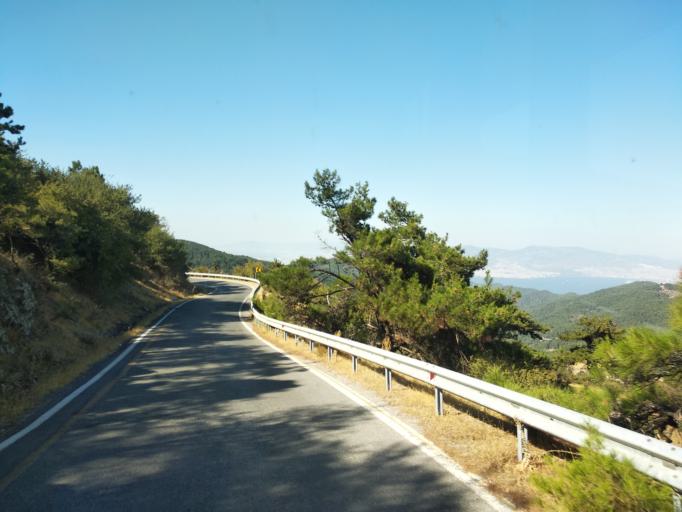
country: TR
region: Izmir
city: Gaziemir
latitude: 38.3232
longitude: 27.0071
